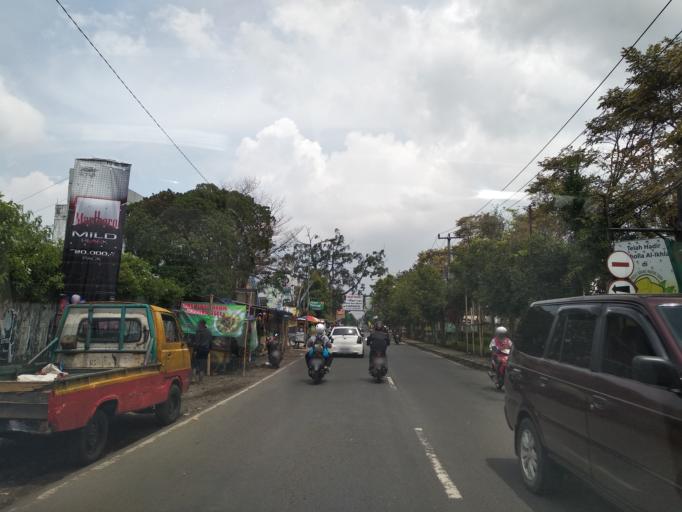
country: ID
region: West Java
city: Lembang
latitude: -6.8166
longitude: 107.6131
